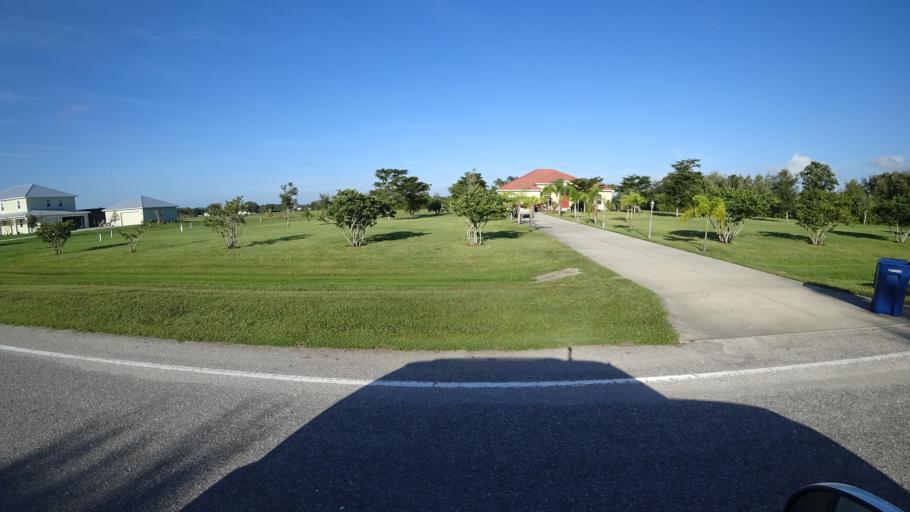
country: US
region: Florida
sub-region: Hillsborough County
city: Sun City Center
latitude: 27.5675
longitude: -82.3531
